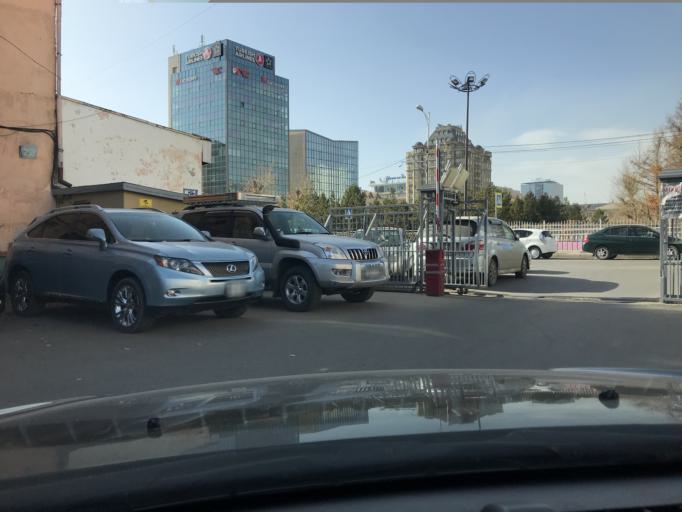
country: MN
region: Ulaanbaatar
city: Ulaanbaatar
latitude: 47.9189
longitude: 106.9102
